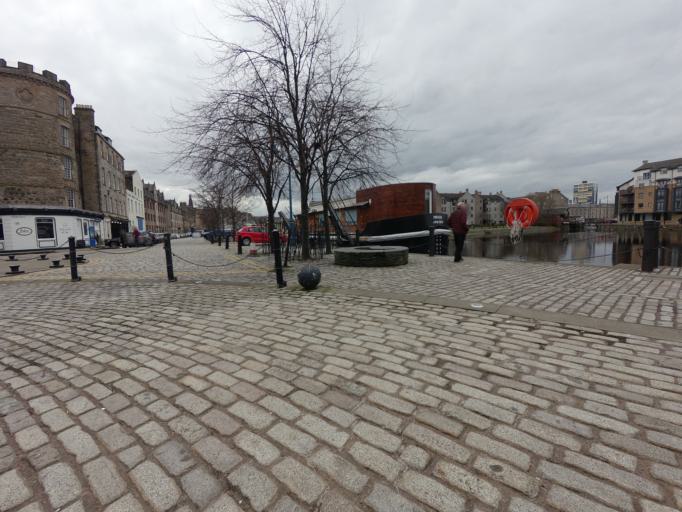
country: GB
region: Scotland
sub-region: West Lothian
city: Seafield
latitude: 55.9780
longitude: -3.1692
